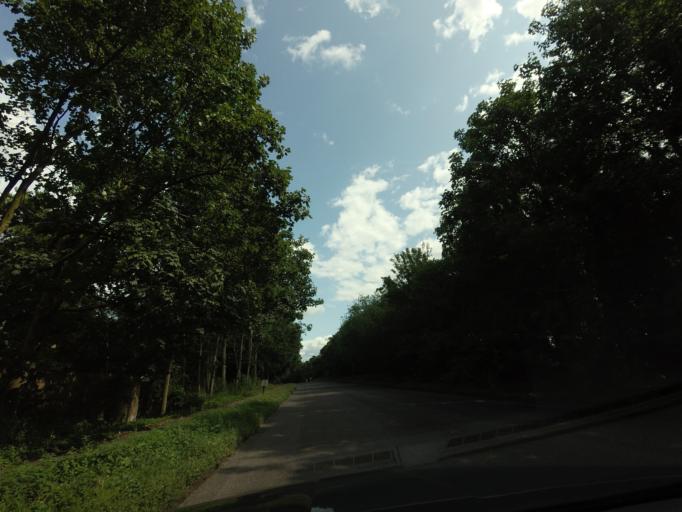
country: GB
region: England
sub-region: Kent
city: Boxley
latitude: 51.2654
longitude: 0.5978
